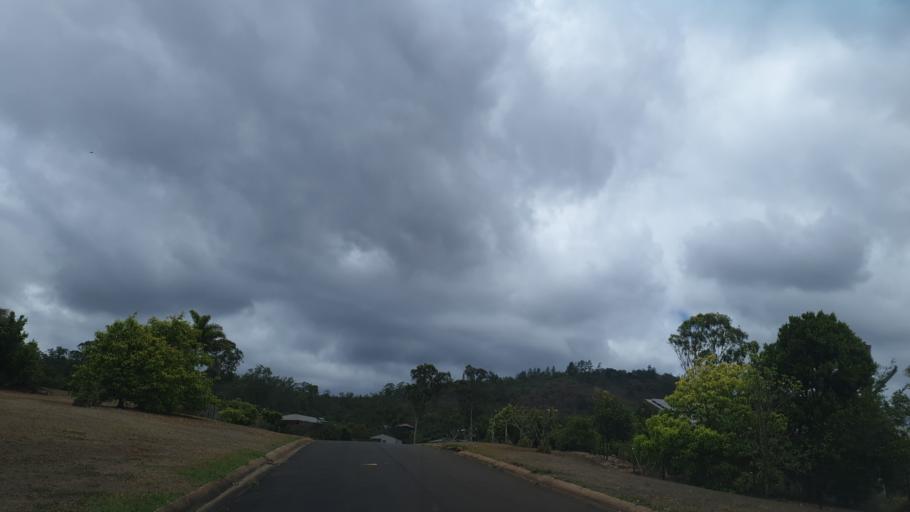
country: AU
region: Queensland
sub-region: Tablelands
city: Tolga
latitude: -17.2101
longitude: 145.4482
